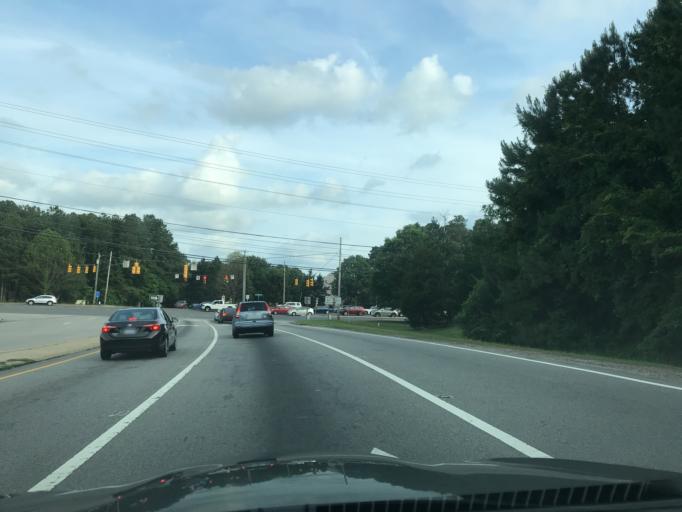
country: US
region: North Carolina
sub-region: Wake County
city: West Raleigh
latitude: 35.8973
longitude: -78.6121
